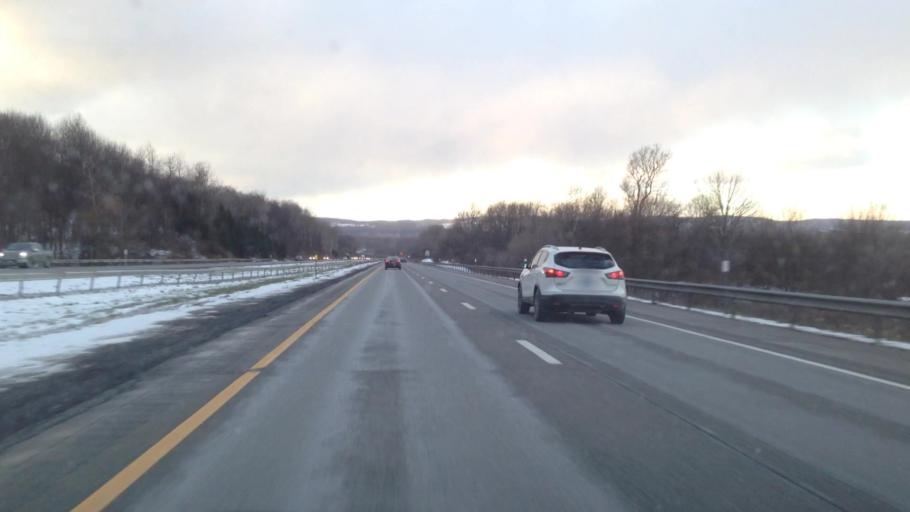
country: US
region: New York
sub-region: Herkimer County
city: Little Falls
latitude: 43.0086
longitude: -74.9077
